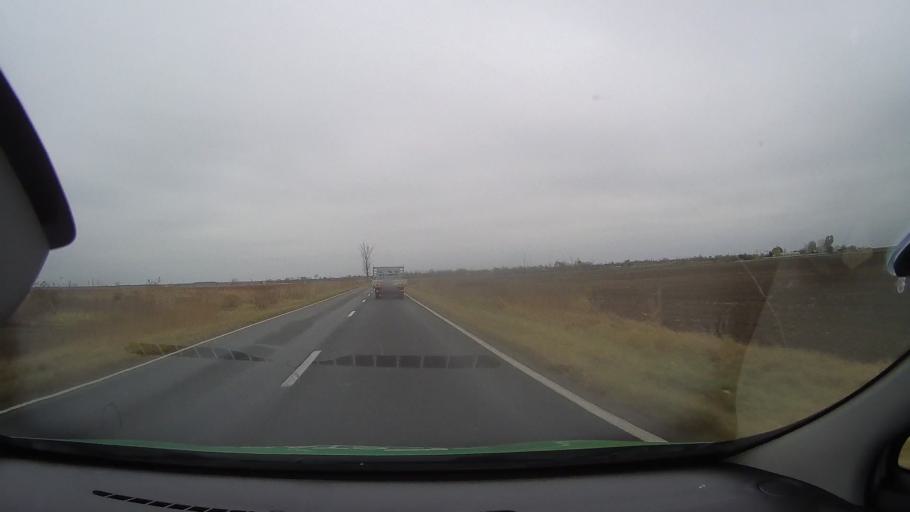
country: RO
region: Ialomita
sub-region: Comuna Scanteia
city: Iazu
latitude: 44.7353
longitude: 27.4330
